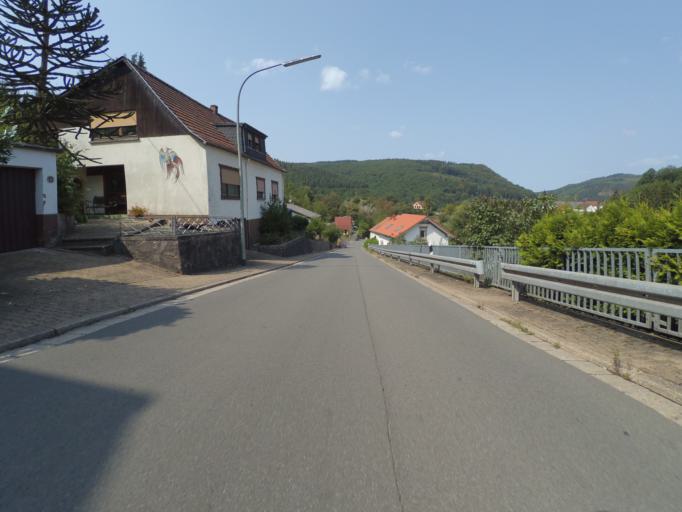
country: DE
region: Saarland
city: Saarhoelzbach
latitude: 49.5119
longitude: 6.6096
